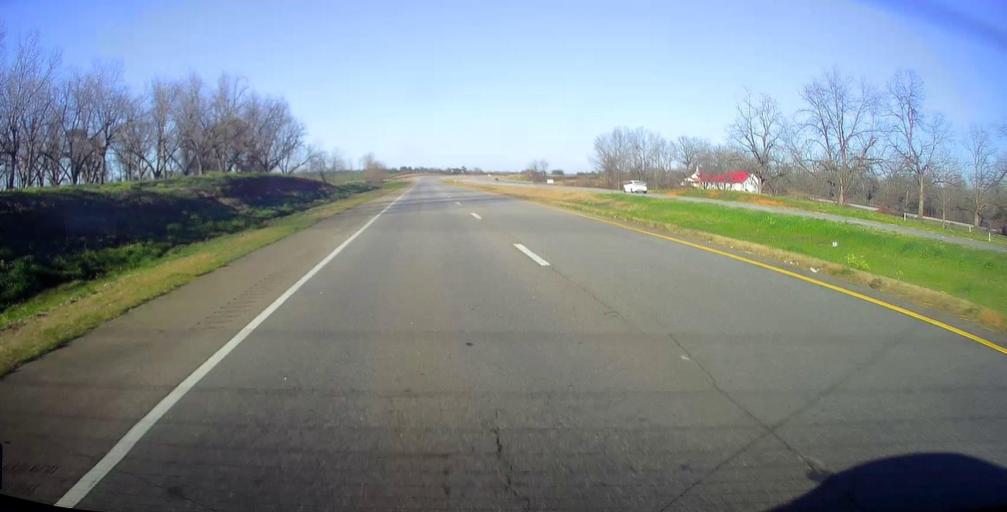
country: US
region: Georgia
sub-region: Sumter County
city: Americus
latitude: 31.9626
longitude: -84.2546
